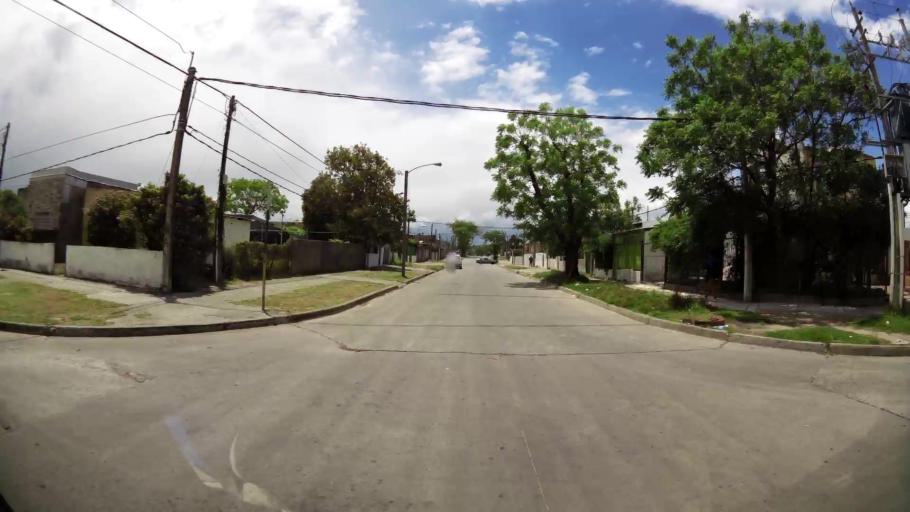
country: UY
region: Montevideo
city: Montevideo
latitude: -34.8670
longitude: -56.1447
